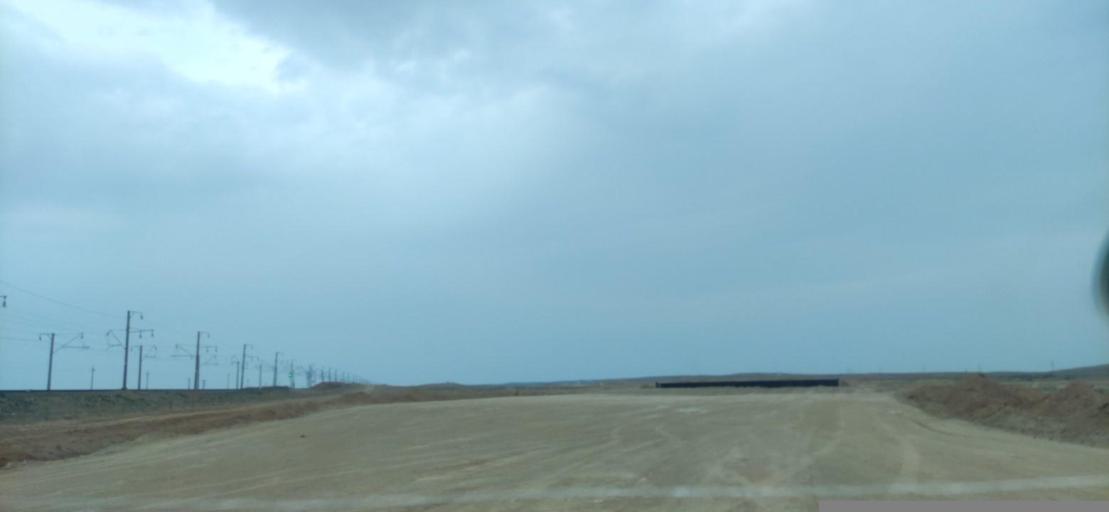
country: KZ
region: Qaraghandy
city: Saryshaghan
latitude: 46.1390
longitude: 73.6057
